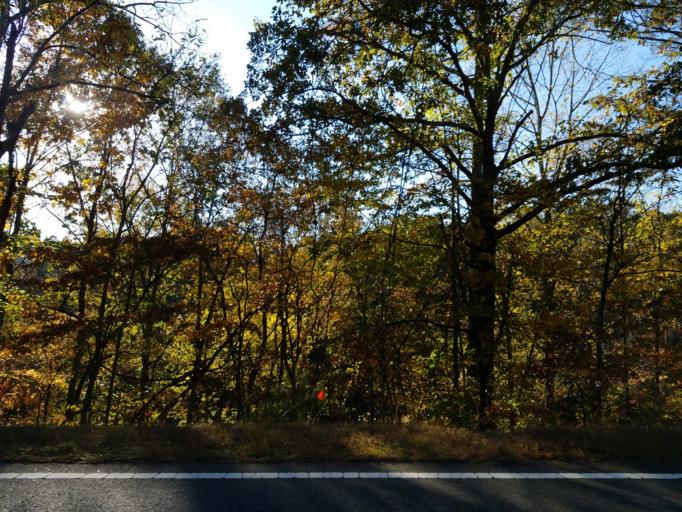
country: US
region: Georgia
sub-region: Pickens County
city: Jasper
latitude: 34.5318
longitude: -84.4784
